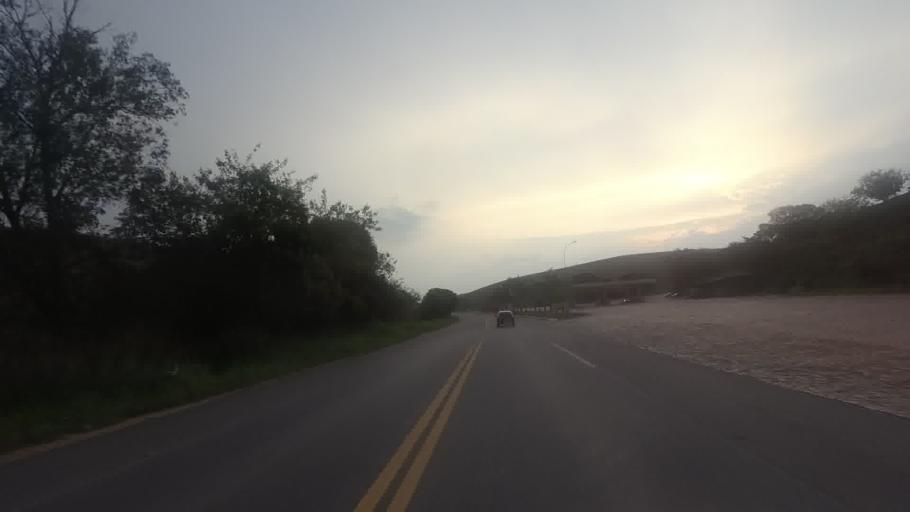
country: BR
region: Rio de Janeiro
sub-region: Carmo
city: Carmo
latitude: -21.7890
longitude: -42.5520
